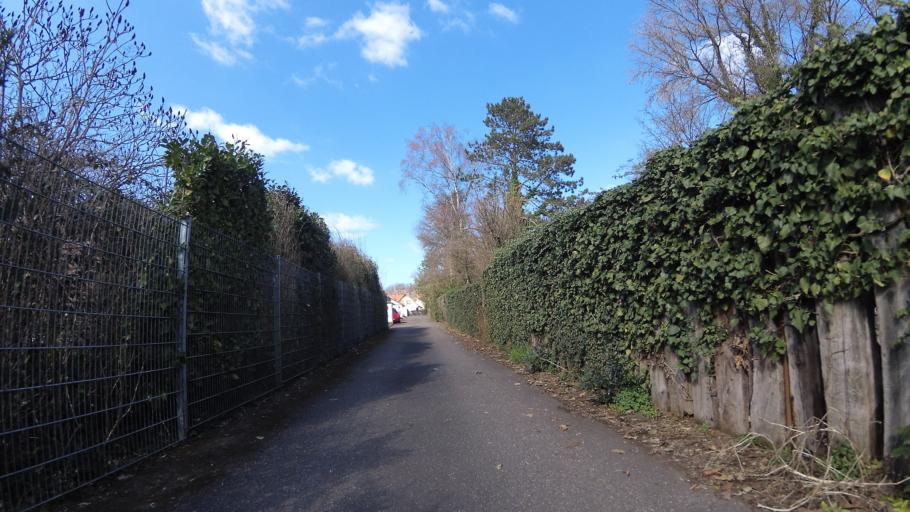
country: DE
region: Saarland
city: Beckingen
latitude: 49.3856
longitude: 6.7123
